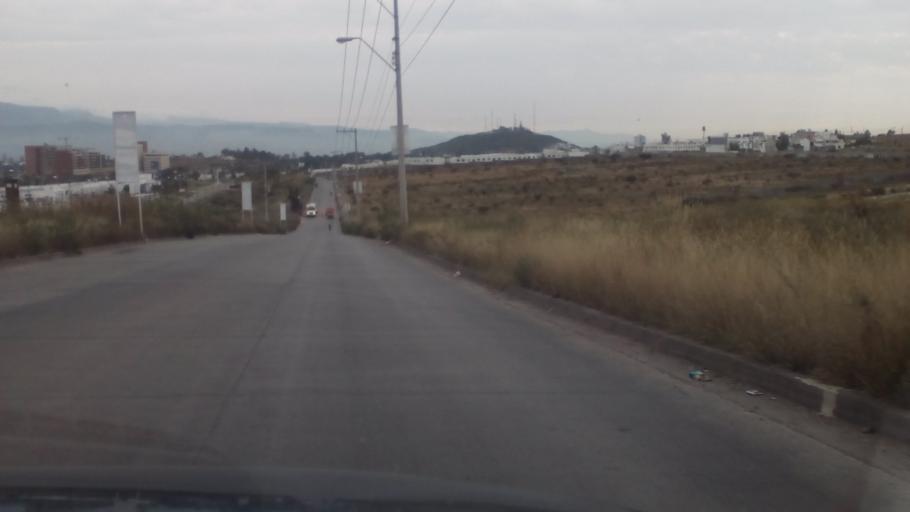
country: MX
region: Guanajuato
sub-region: Leon
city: Fraccionamiento Paseo de las Torres
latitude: 21.1712
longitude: -101.7482
